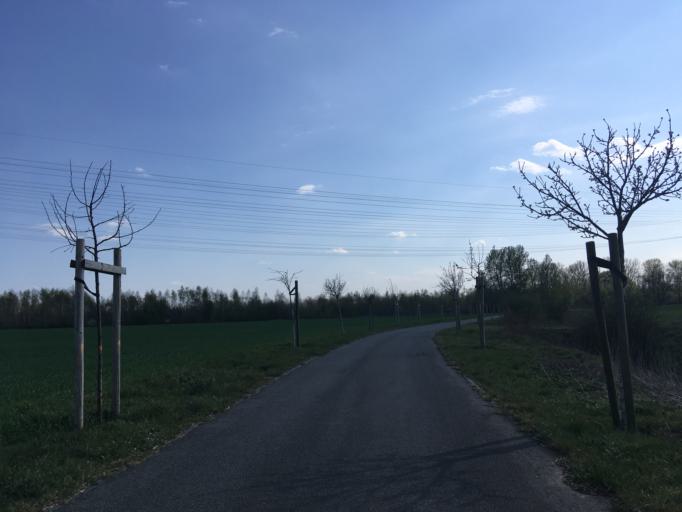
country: DE
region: Berlin
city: Wartenberg
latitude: 52.5915
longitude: 13.5005
